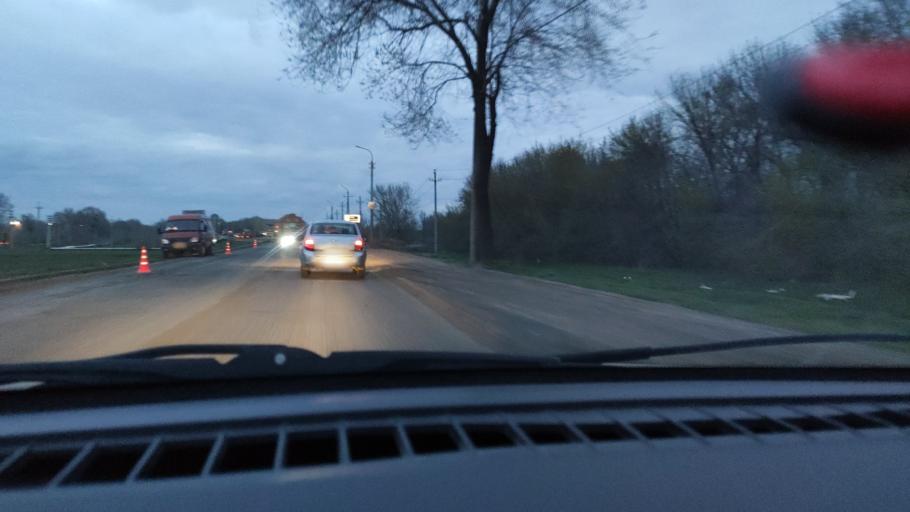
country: RU
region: Orenburg
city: Tatarskaya Kargala
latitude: 51.8676
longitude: 55.1417
